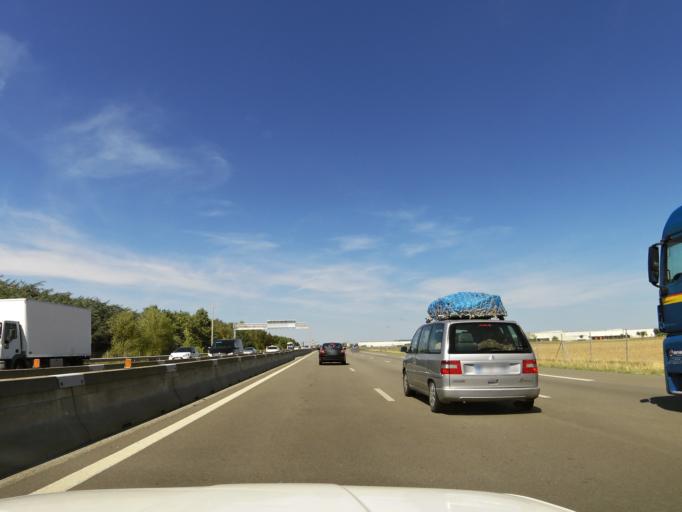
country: FR
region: Rhone-Alpes
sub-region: Departement de la Drome
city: Andancette
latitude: 45.2569
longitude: 4.8360
